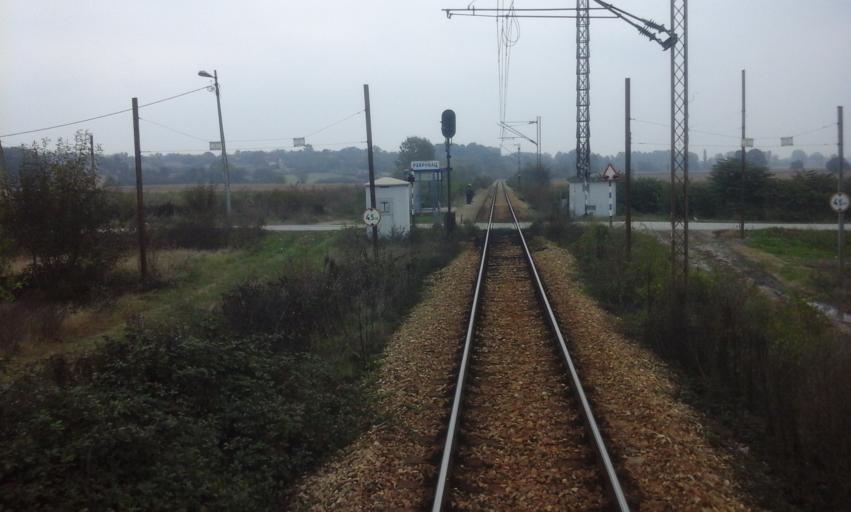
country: RS
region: Central Serbia
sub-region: Belgrade
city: Mladenovac
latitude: 44.3847
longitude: 20.7742
